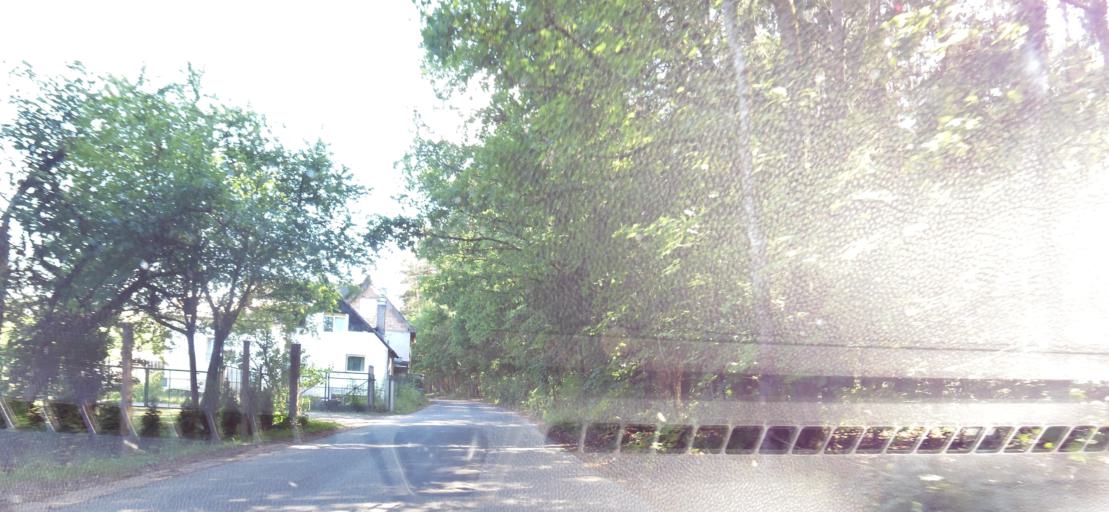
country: LT
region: Vilnius County
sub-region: Vilnius
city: Fabijoniskes
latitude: 54.8231
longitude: 25.3199
